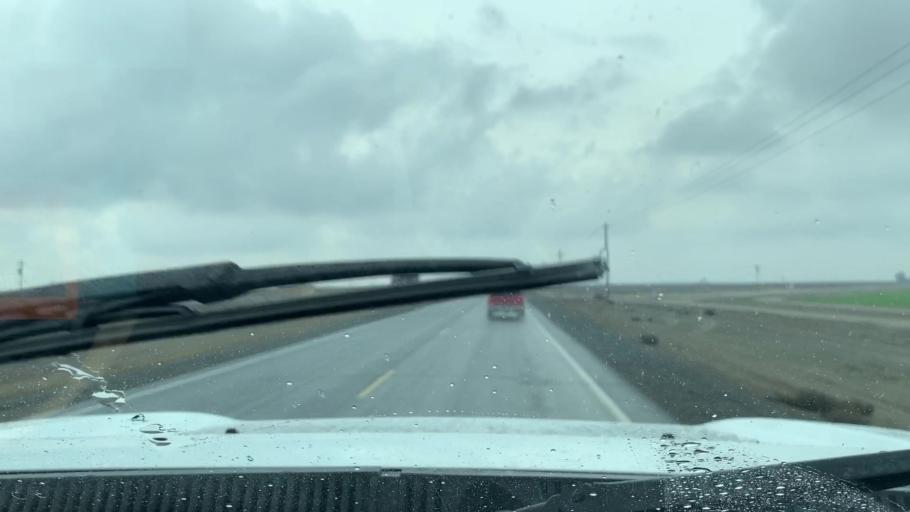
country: US
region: California
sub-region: Kings County
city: Corcoran
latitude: 36.0090
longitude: -119.4912
